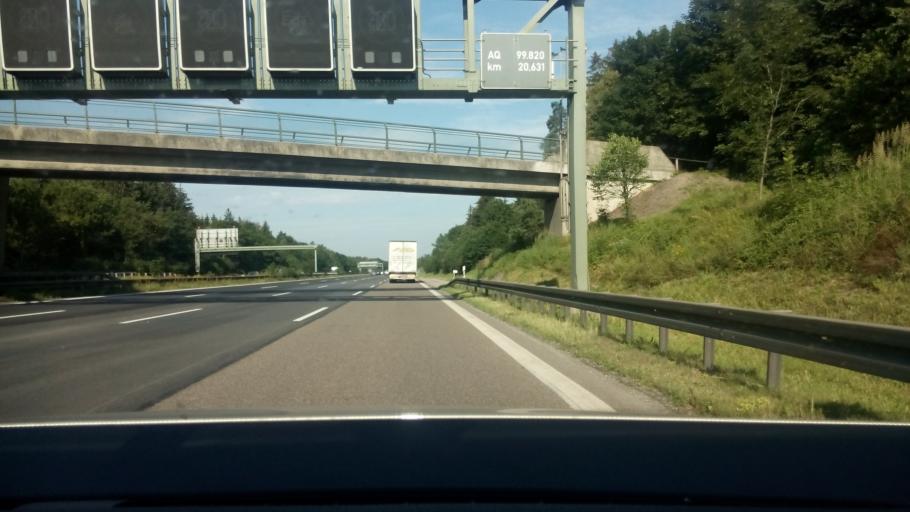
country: DE
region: Bavaria
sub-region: Upper Bavaria
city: Oberschleissheim
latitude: 48.2285
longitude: 11.5831
